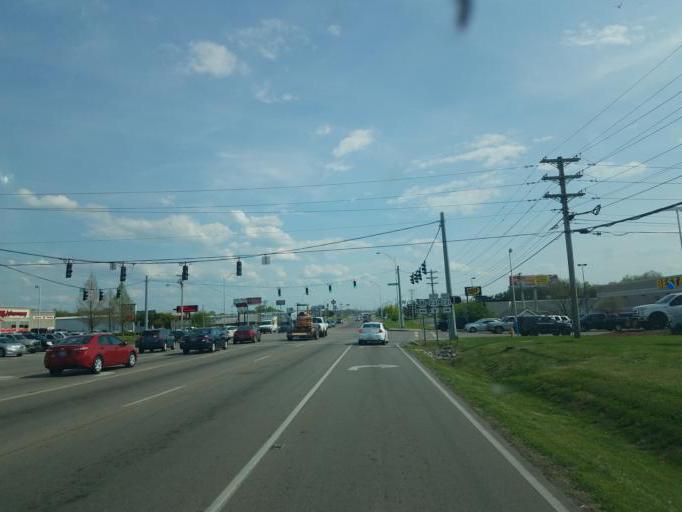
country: US
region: Kentucky
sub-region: Warren County
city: Bowling Green
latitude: 36.9550
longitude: -86.4272
